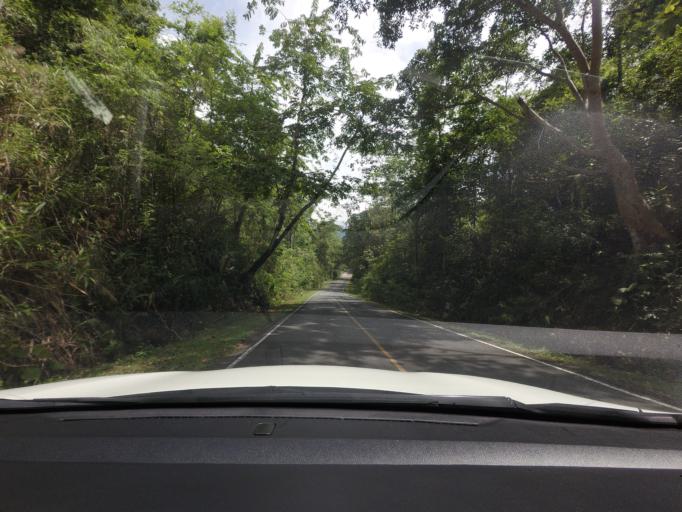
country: TH
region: Nakhon Nayok
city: Pak Phli
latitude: 14.2927
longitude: 101.3956
